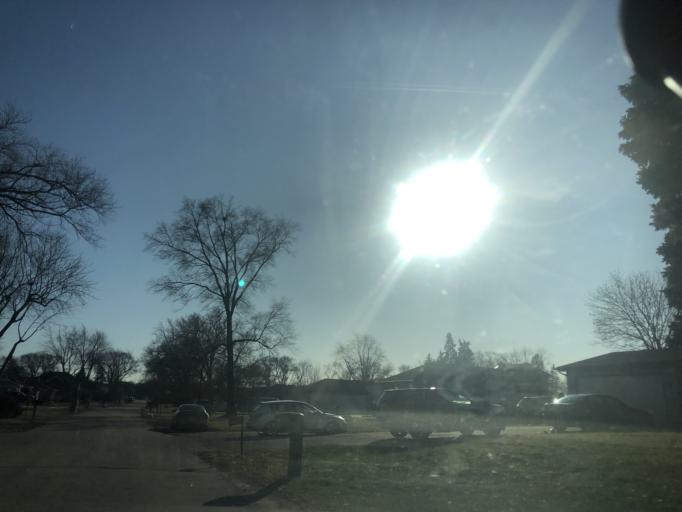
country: US
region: Illinois
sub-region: DuPage County
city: Addison
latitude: 41.9429
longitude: -88.0063
